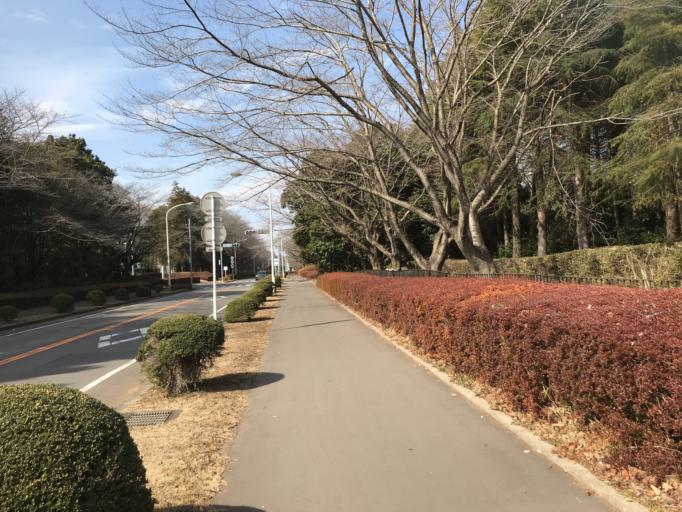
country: JP
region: Ibaraki
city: Naka
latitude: 36.0304
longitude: 140.1039
